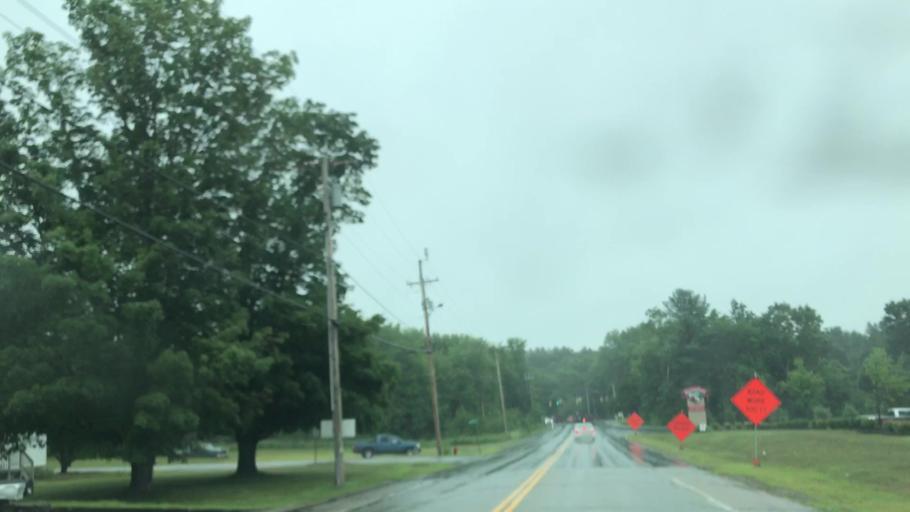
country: US
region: Maine
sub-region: York County
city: North Berwick
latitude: 43.2995
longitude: -70.7448
